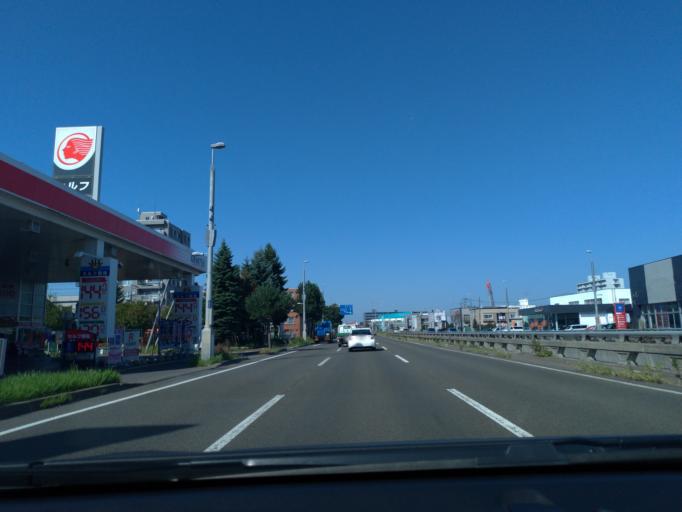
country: JP
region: Hokkaido
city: Sapporo
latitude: 43.1040
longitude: 141.3446
